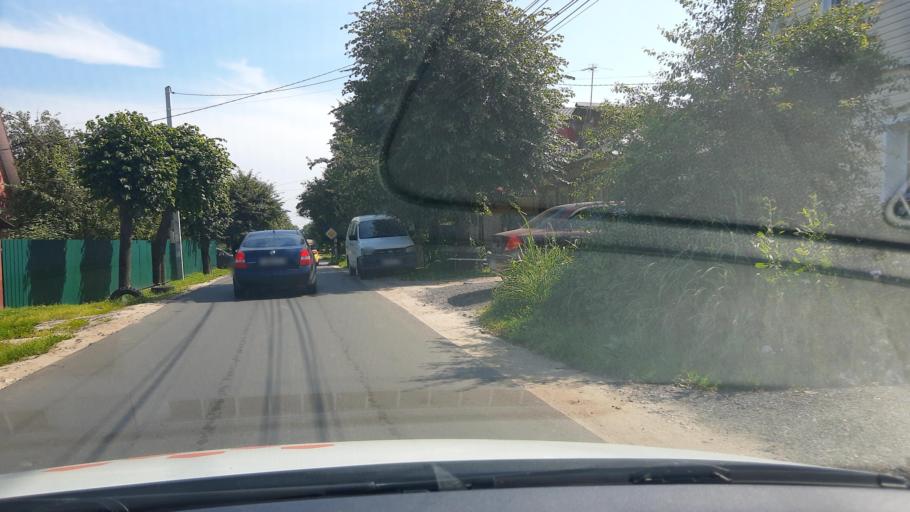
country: RU
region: Moskovskaya
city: Bronnitsy
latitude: 55.4258
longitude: 38.2564
